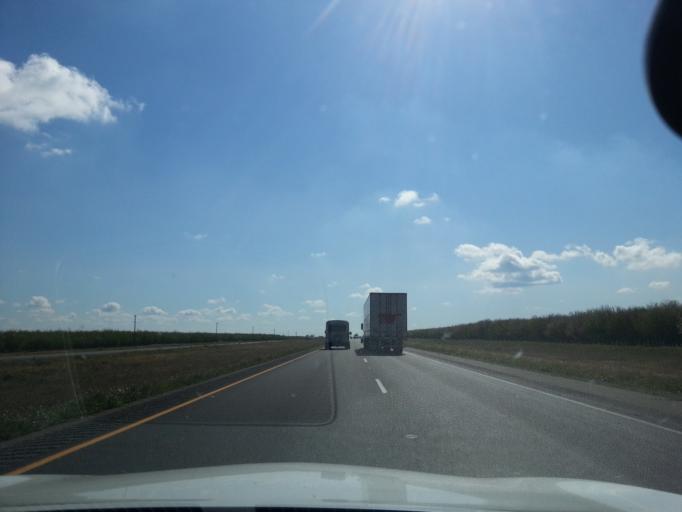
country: US
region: California
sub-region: Fresno County
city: San Joaquin
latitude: 36.4115
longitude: -120.3727
